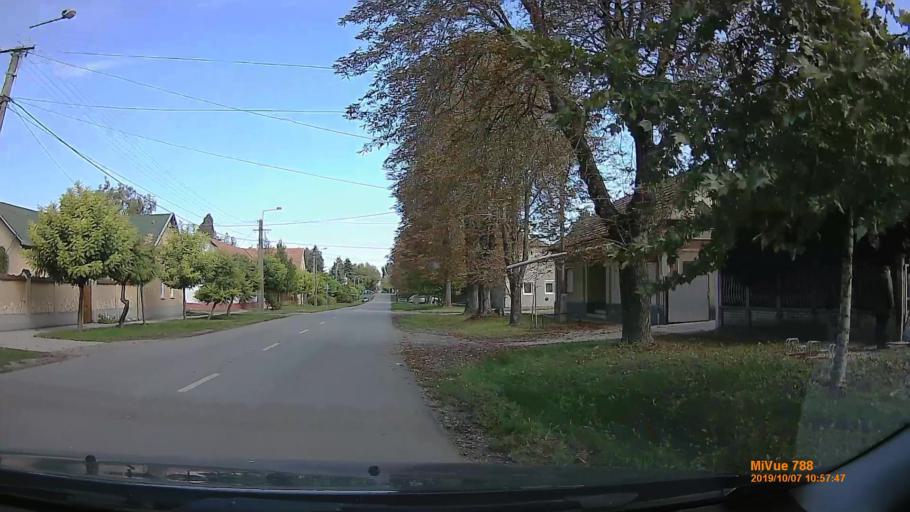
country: HU
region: Bekes
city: Kondoros
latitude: 46.7561
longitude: 20.7976
